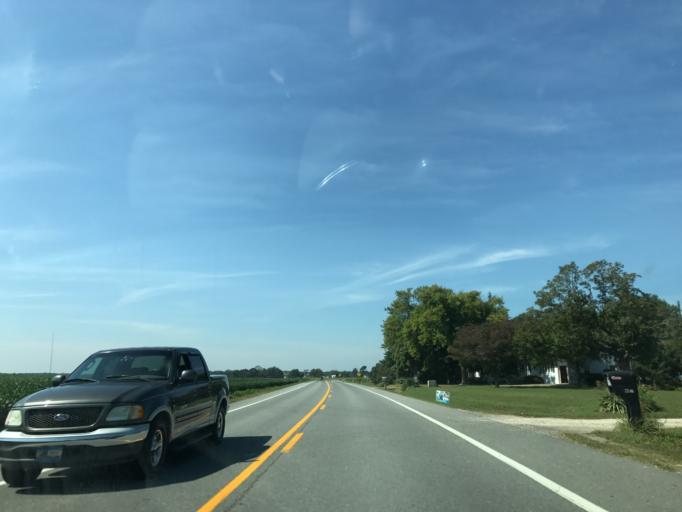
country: US
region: Delaware
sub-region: New Castle County
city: Townsend
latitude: 39.3080
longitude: -75.8149
